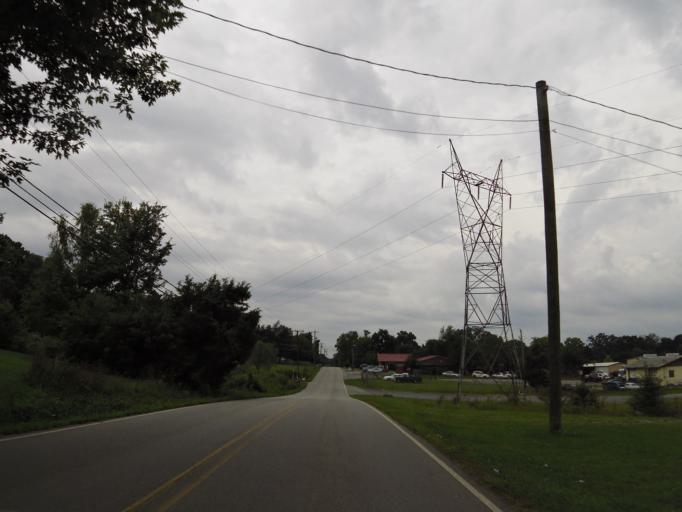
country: US
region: Tennessee
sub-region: Blount County
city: Eagleton Village
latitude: 35.8175
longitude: -83.9547
